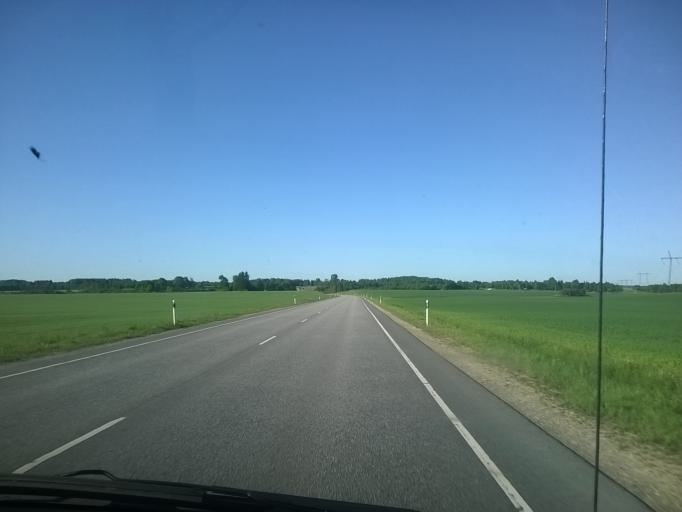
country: EE
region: Tartu
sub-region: Elva linn
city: Elva
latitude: 58.2012
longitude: 26.3554
